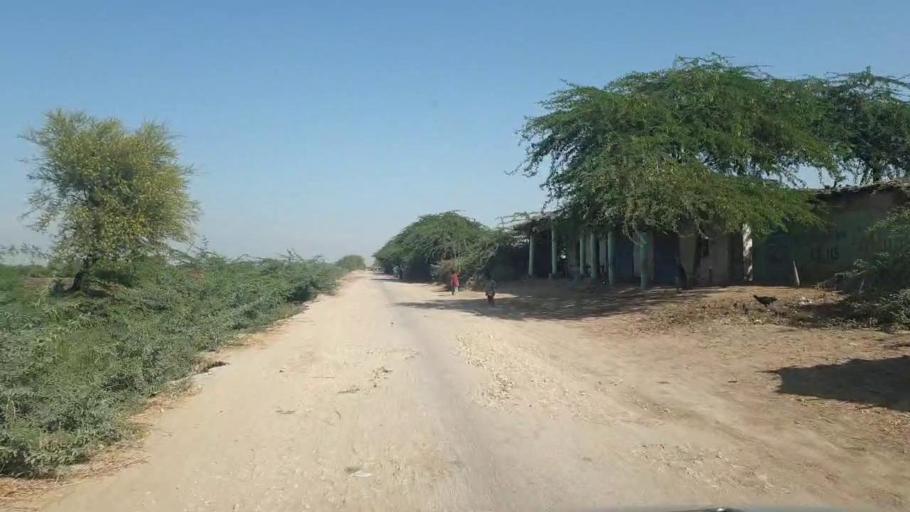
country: PK
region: Sindh
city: Tando Bago
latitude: 24.7983
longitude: 68.9764
